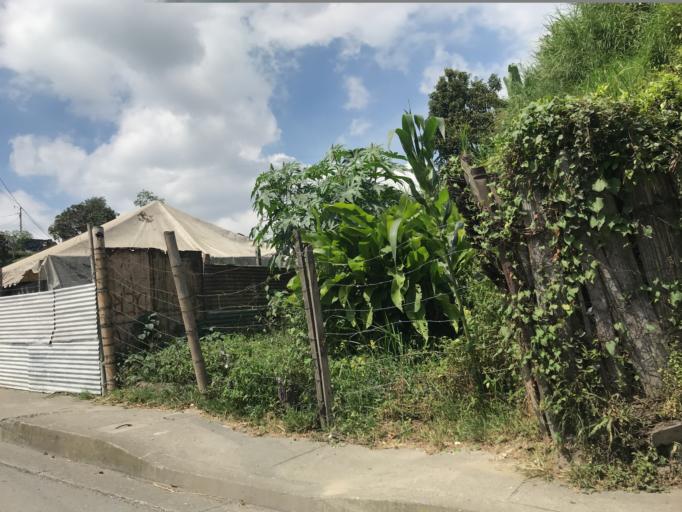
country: CO
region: Quindio
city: Calarca
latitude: 4.5241
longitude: -75.6382
